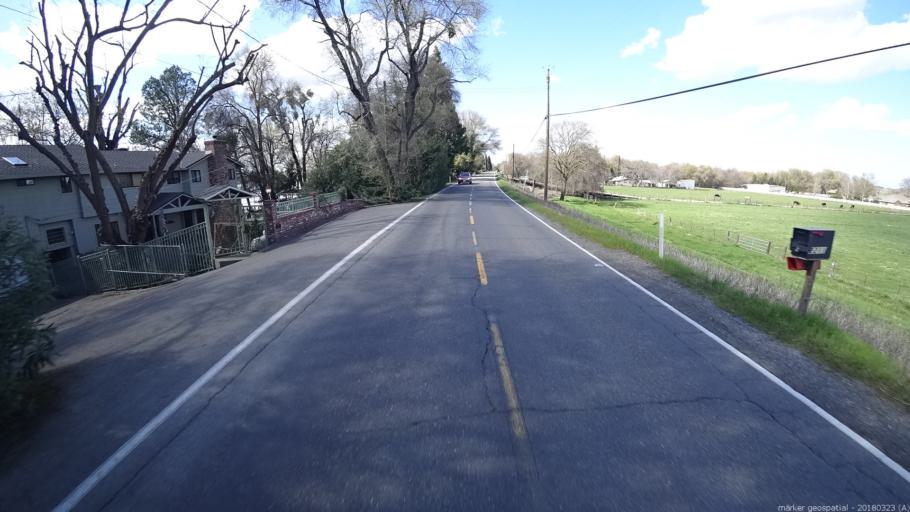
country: US
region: California
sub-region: Yolo County
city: West Sacramento
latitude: 38.6026
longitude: -121.5513
